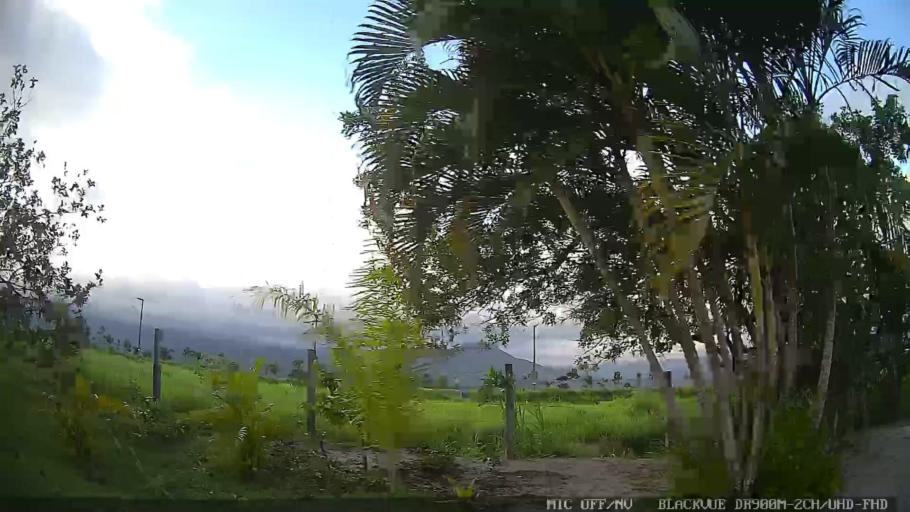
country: BR
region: Sao Paulo
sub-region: Caraguatatuba
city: Caraguatatuba
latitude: -23.6606
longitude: -45.4454
